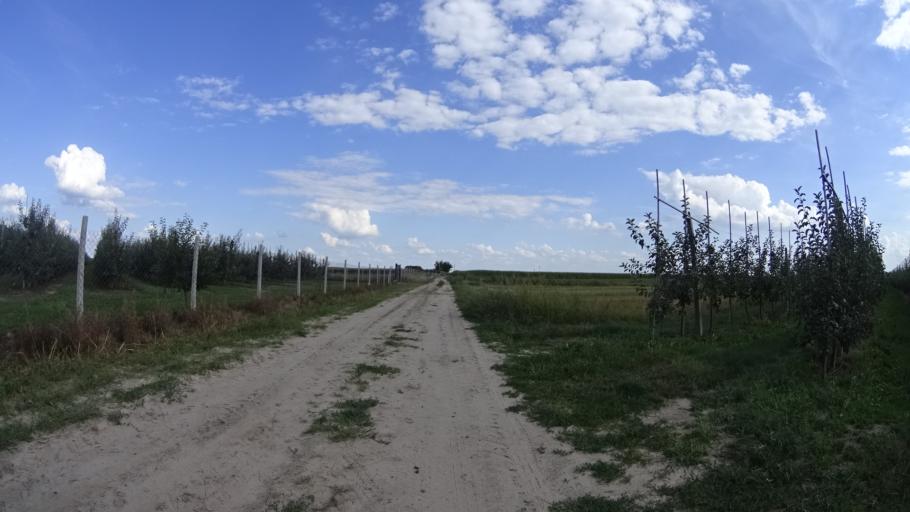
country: PL
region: Masovian Voivodeship
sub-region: Powiat bialobrzeski
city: Wysmierzyce
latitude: 51.6711
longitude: 20.8013
